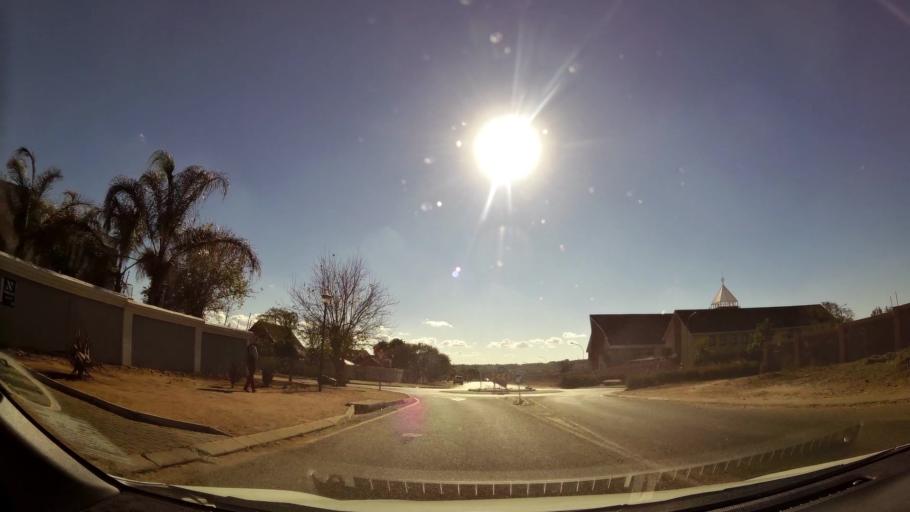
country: ZA
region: Limpopo
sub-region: Capricorn District Municipality
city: Polokwane
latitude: -23.9108
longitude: 29.5038
